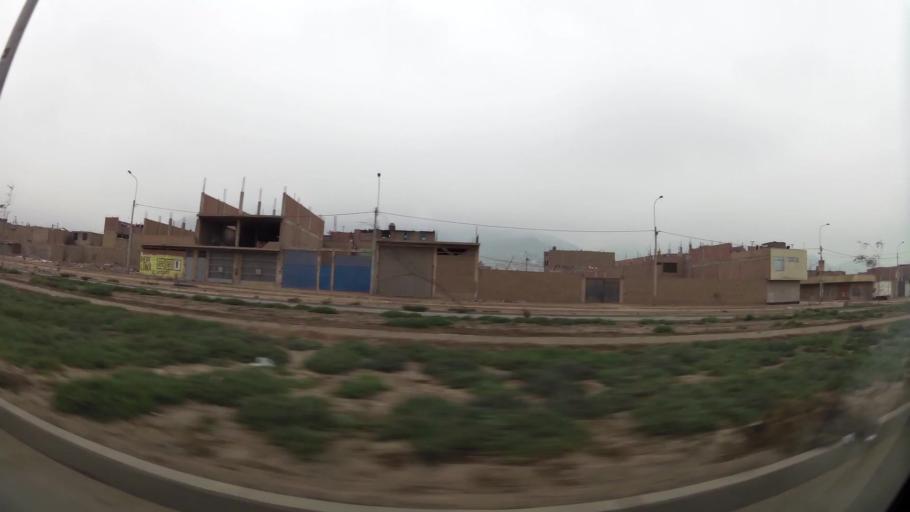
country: PE
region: Lima
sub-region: Lima
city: Urb. Santo Domingo
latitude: -11.8824
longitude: -77.0261
